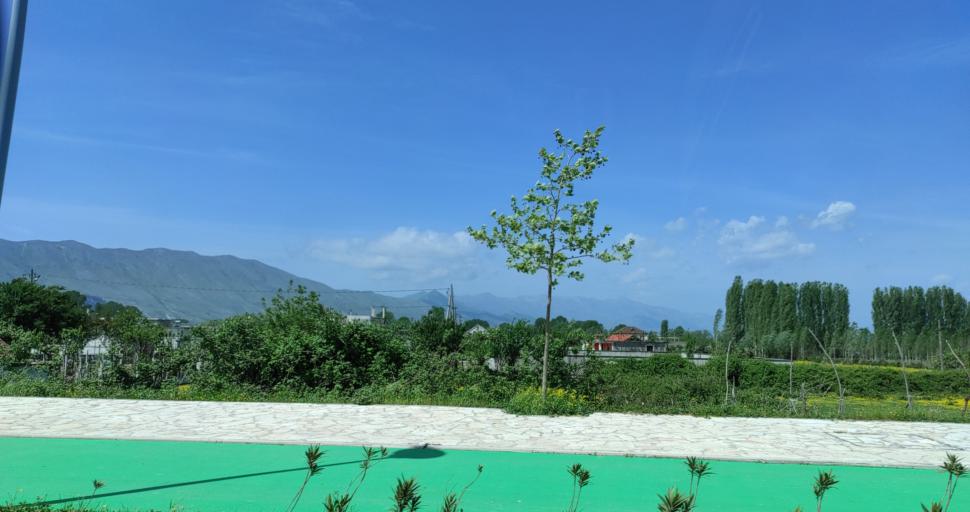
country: AL
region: Shkoder
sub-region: Rrethi i Shkodres
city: Shkoder
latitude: 42.0792
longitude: 19.4922
